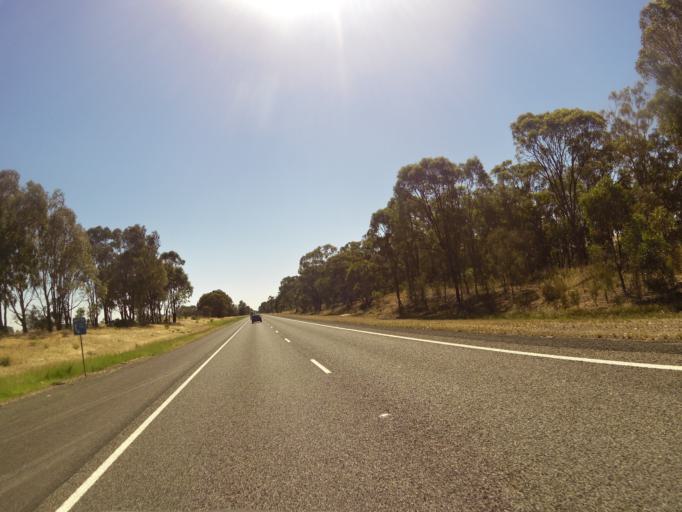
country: AU
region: Victoria
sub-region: Greater Shepparton
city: Shepparton
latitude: -36.8719
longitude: 145.2846
